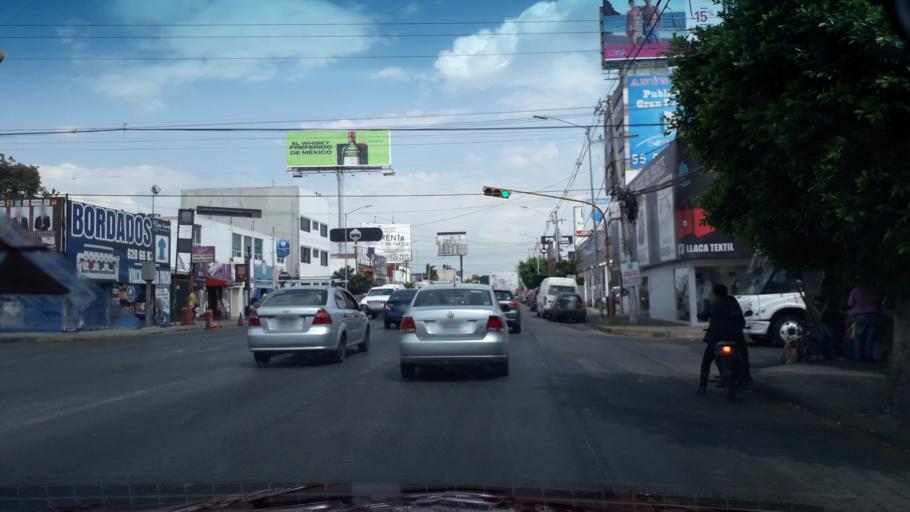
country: MX
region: Puebla
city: Puebla
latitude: 19.0450
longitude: -98.2299
